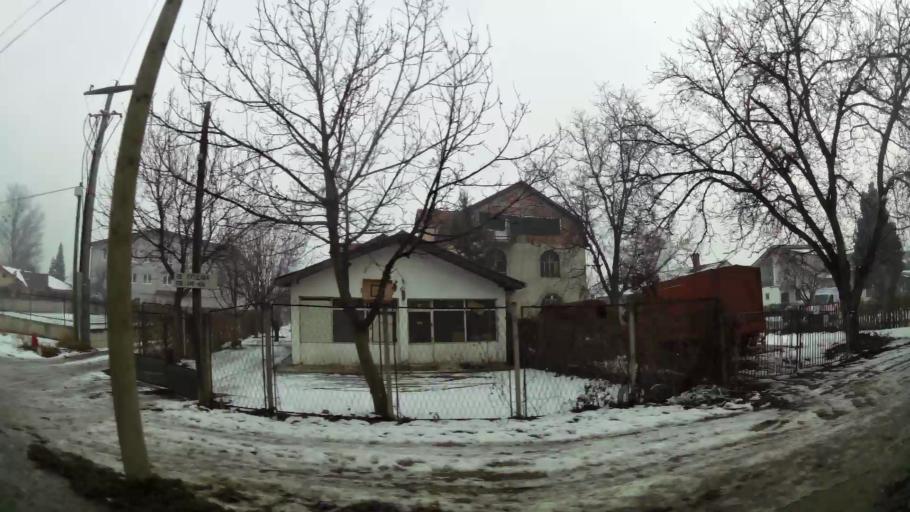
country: MK
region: Ilinden
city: Idrizovo
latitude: 41.9546
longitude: 21.5767
